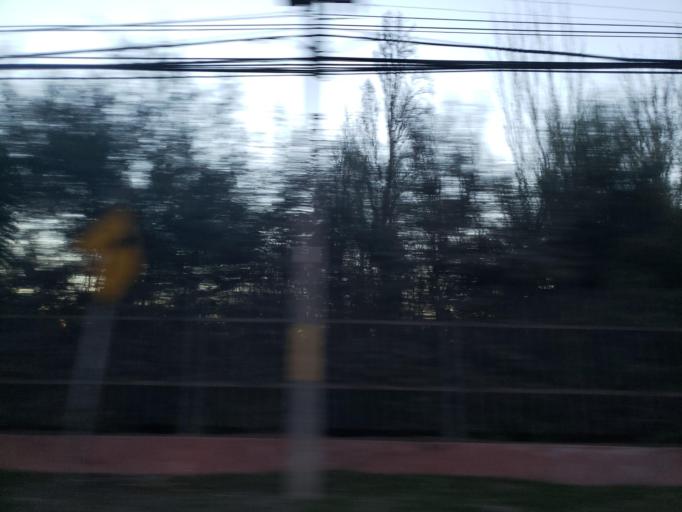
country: CL
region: Santiago Metropolitan
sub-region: Provincia de Talagante
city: Talagante
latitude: -33.6769
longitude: -70.9542
